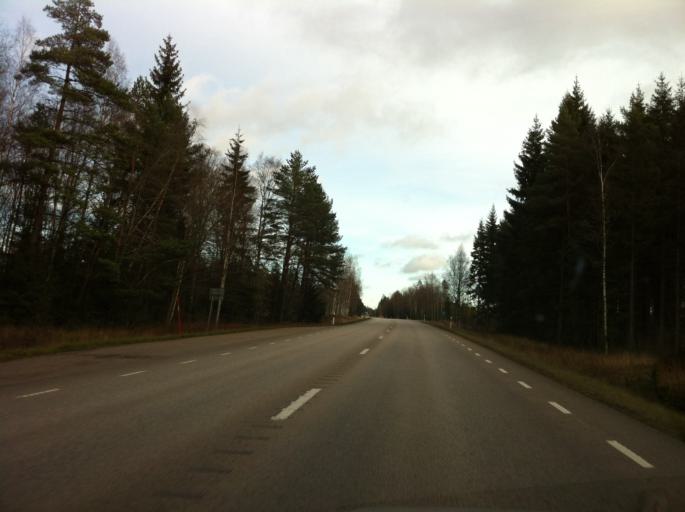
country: SE
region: Kronoberg
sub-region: Uppvidinge Kommun
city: Aseda
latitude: 57.1492
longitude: 15.3034
